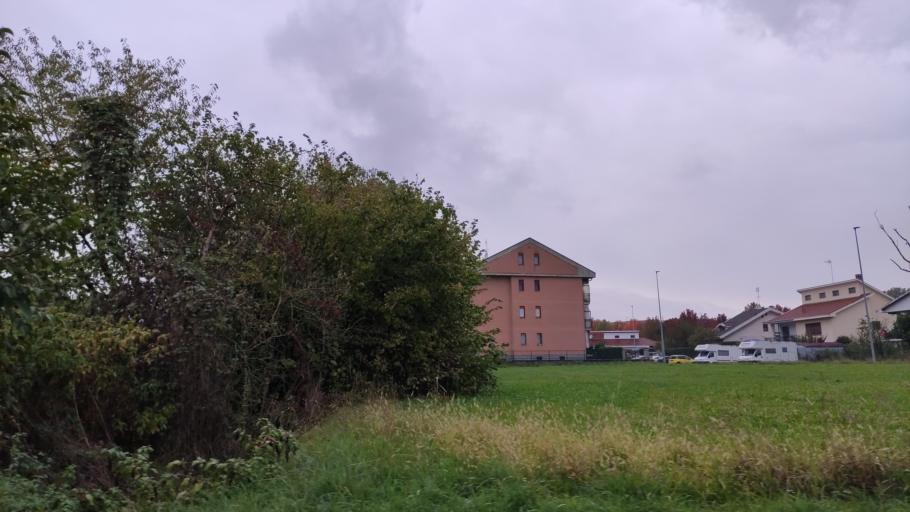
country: IT
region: Piedmont
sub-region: Provincia di Torino
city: Settimo Torinese
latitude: 45.1457
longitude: 7.7687
